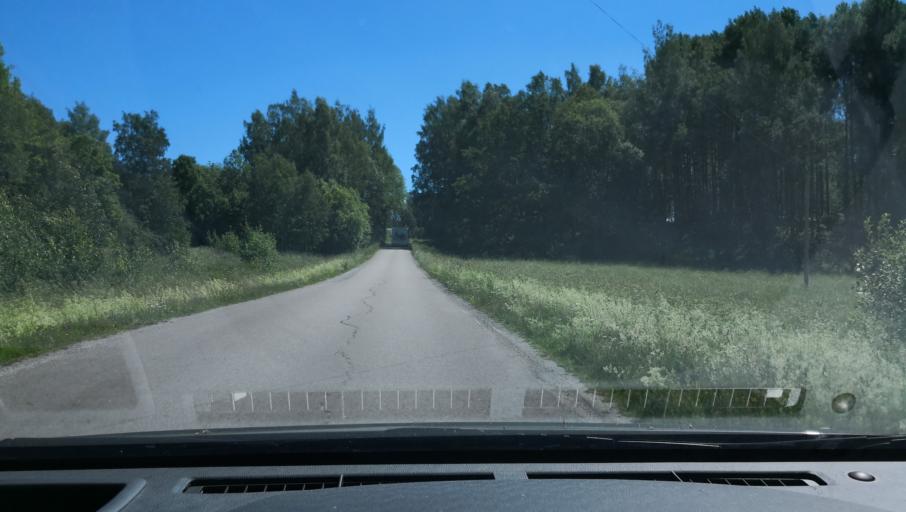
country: SE
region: Vaestmanland
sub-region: Arboga Kommun
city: Tyringe
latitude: 59.3855
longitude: 15.9448
